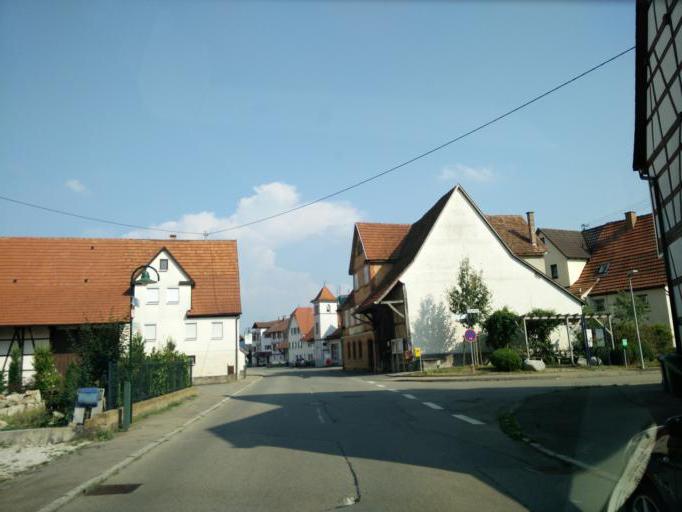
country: DE
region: Baden-Wuerttemberg
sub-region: Tuebingen Region
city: Gomaringen
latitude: 48.4733
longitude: 9.0845
